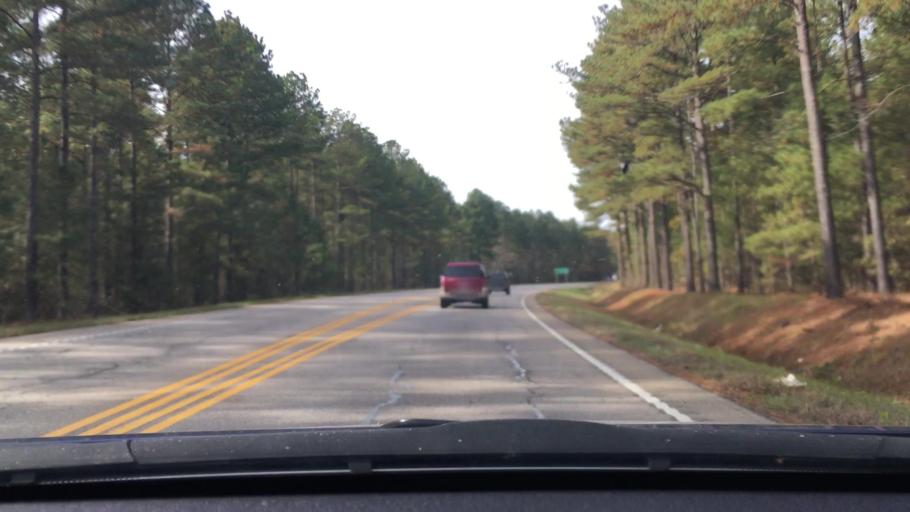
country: US
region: South Carolina
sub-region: Sumter County
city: Cherryvale
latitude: 33.9434
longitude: -80.4913
